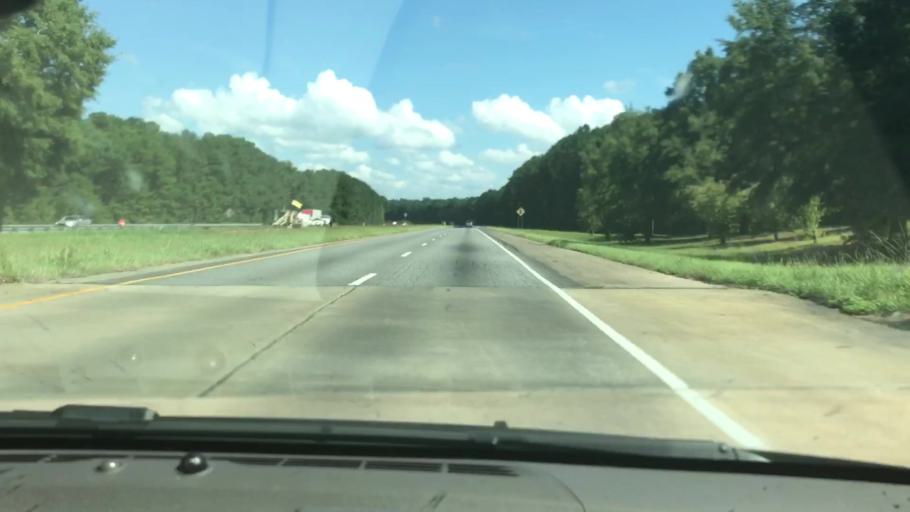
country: US
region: Georgia
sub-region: Harris County
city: Hamilton
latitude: 32.7475
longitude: -85.0175
